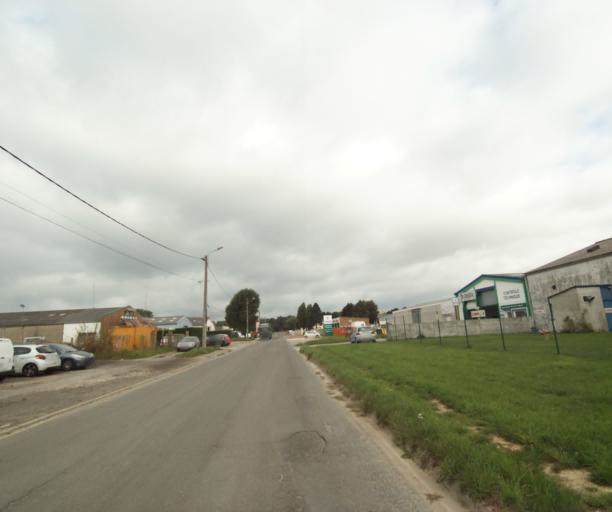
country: FR
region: Nord-Pas-de-Calais
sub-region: Departement du Pas-de-Calais
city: Etaples
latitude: 50.5198
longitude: 1.6620
